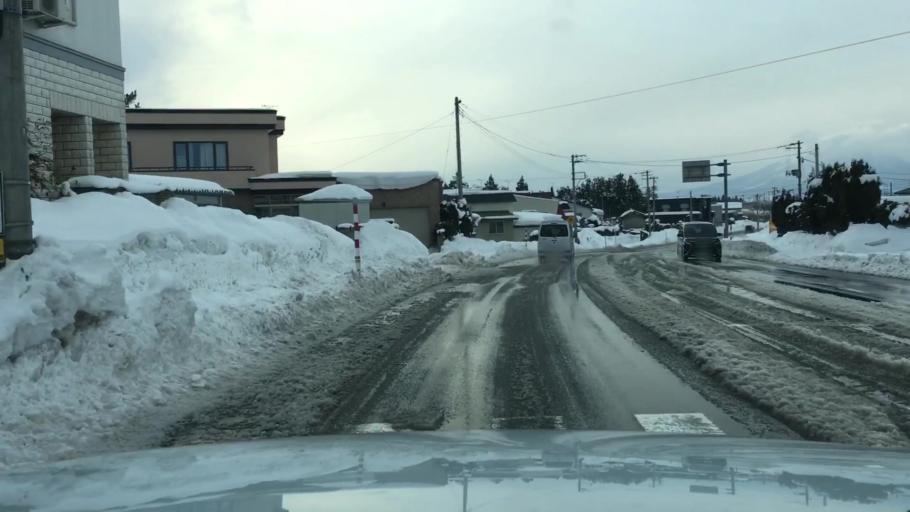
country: JP
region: Aomori
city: Kuroishi
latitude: 40.5912
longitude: 140.5569
